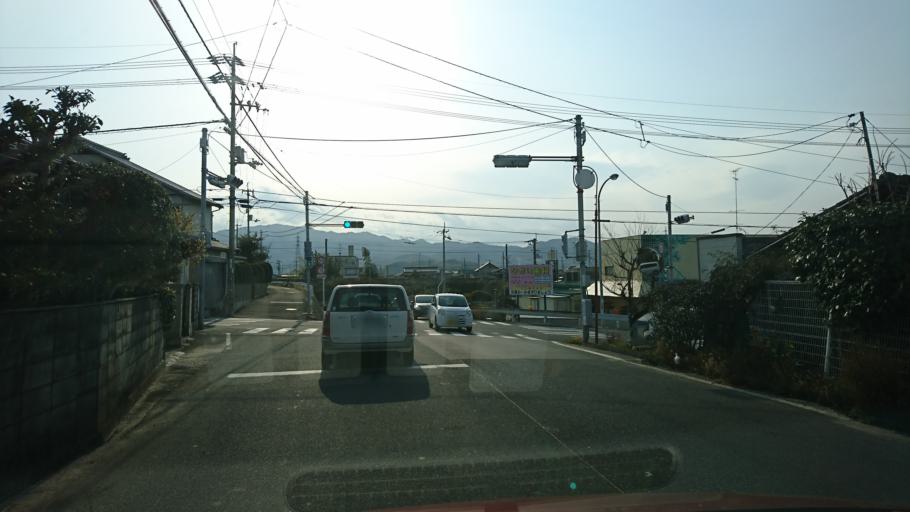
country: JP
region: Ehime
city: Saijo
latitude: 34.0304
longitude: 133.0157
